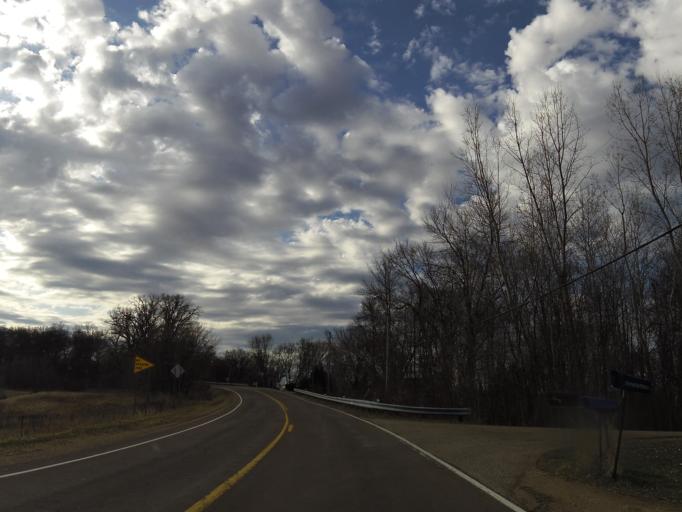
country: US
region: Minnesota
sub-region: Dakota County
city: Hastings
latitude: 44.7588
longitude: -92.8451
